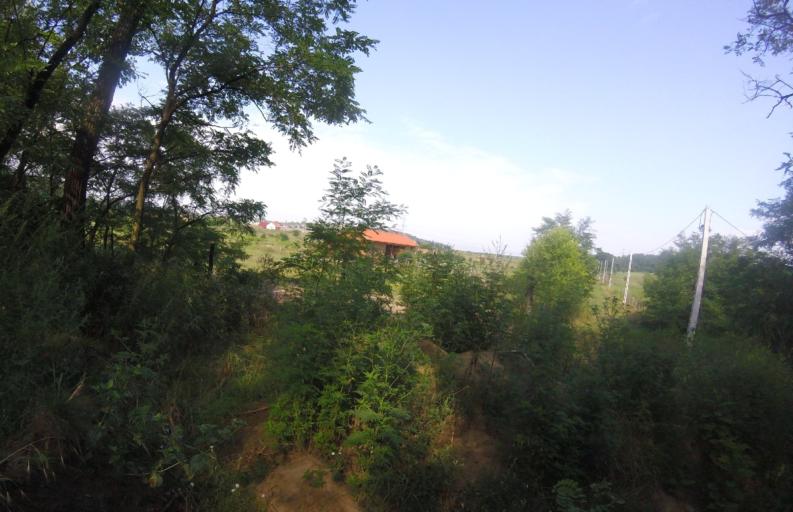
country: HU
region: Pest
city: Fot
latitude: 47.6392
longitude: 19.2162
